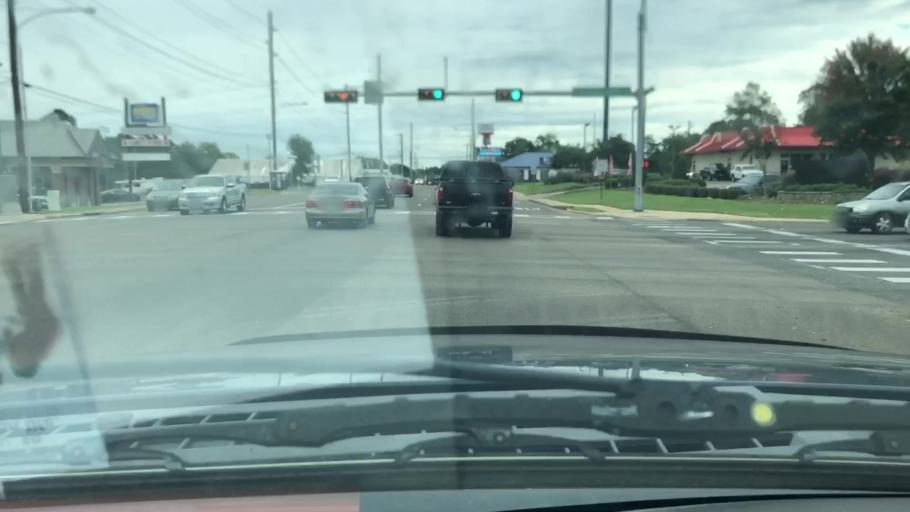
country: US
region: Texas
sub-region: Bowie County
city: Texarkana
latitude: 33.4349
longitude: -94.0630
